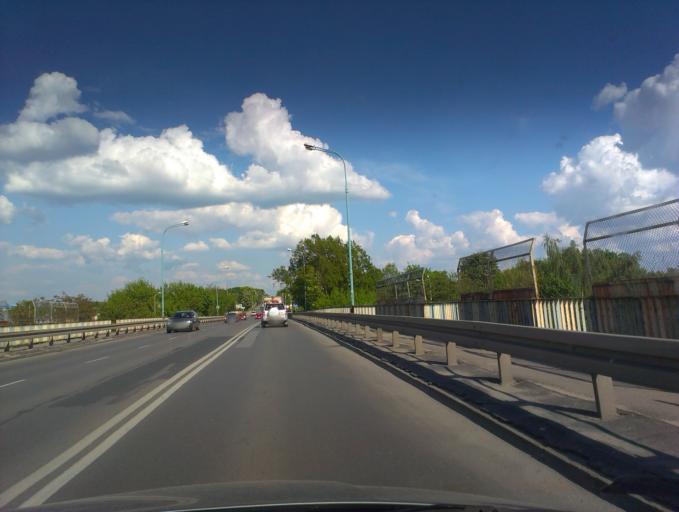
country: PL
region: Masovian Voivodeship
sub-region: Radom
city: Radom
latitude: 51.3991
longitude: 21.1738
